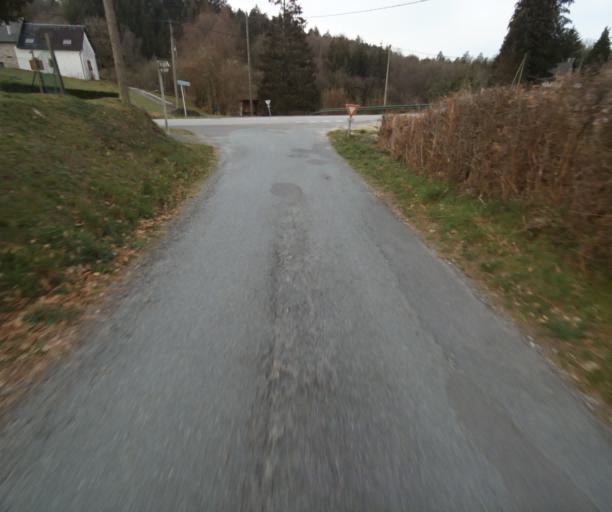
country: FR
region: Limousin
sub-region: Departement de la Correze
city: Correze
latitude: 45.4231
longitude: 1.8454
